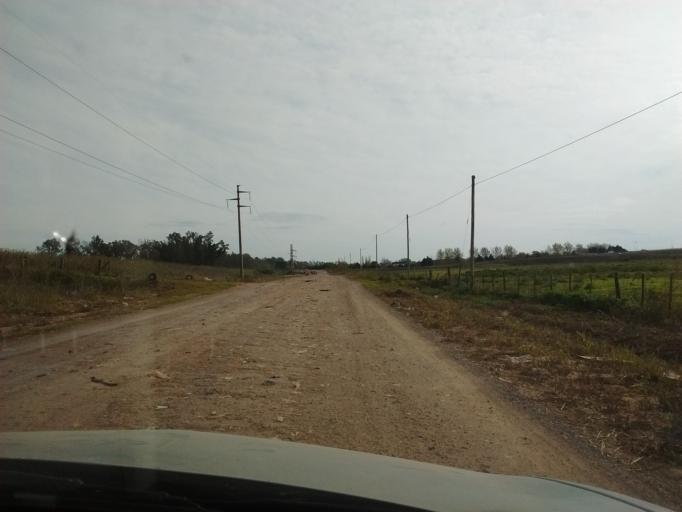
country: AR
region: Santa Fe
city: Funes
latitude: -32.9426
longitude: -60.8151
